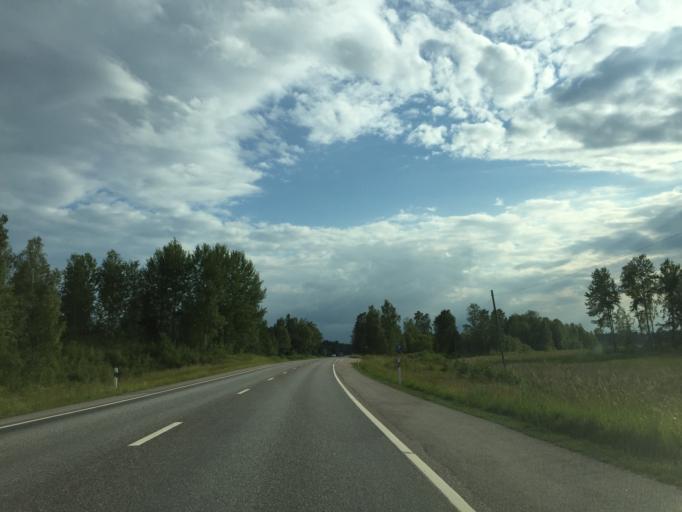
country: SE
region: OErebro
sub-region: Lindesbergs Kommun
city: Fellingsbro
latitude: 59.3626
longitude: 15.6930
